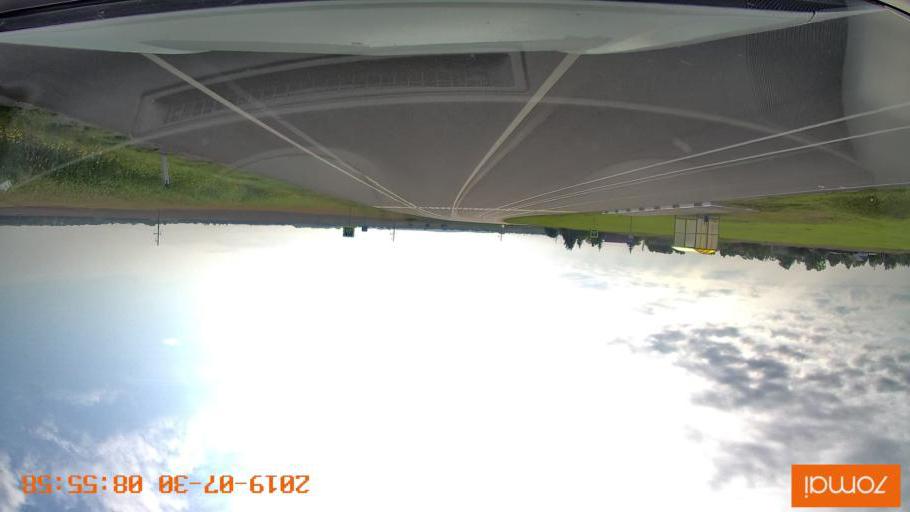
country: RU
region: Kaliningrad
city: Gusev
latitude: 54.5987
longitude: 22.0644
